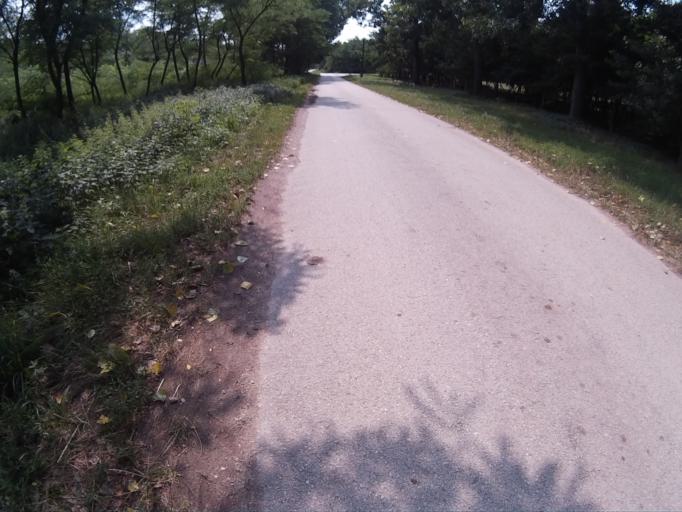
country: HU
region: Veszprem
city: Papa
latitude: 47.2955
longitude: 17.5974
